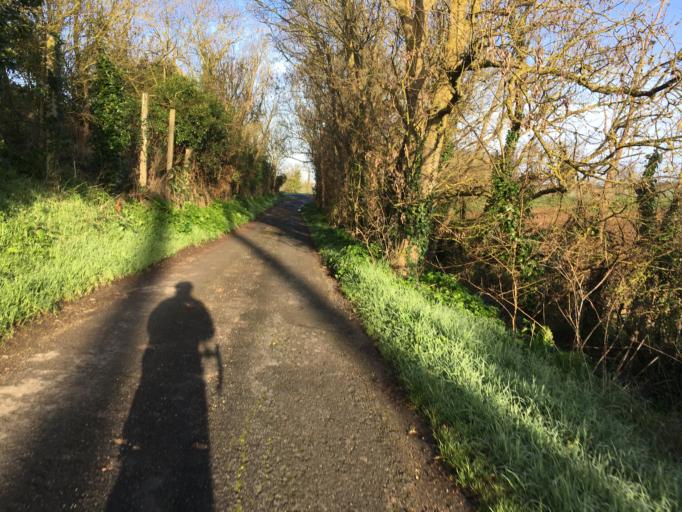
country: FR
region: Poitou-Charentes
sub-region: Departement de la Charente-Maritime
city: Nieul-sur-Mer
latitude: 46.1988
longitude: -1.1800
